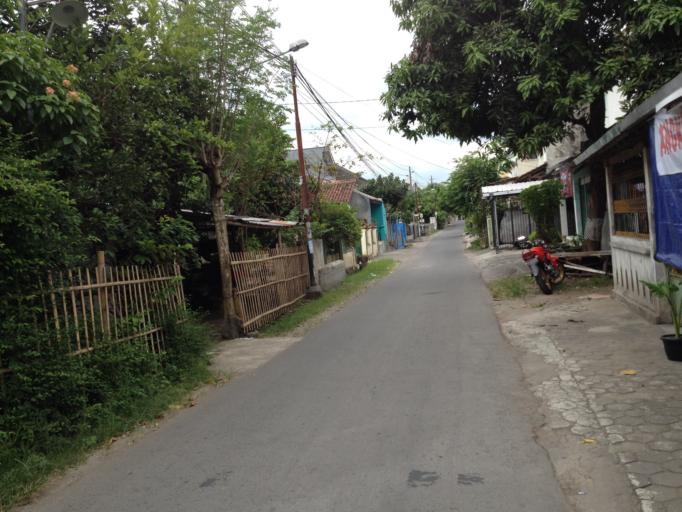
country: ID
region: Daerah Istimewa Yogyakarta
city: Yogyakarta
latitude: -7.8073
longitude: 110.3983
